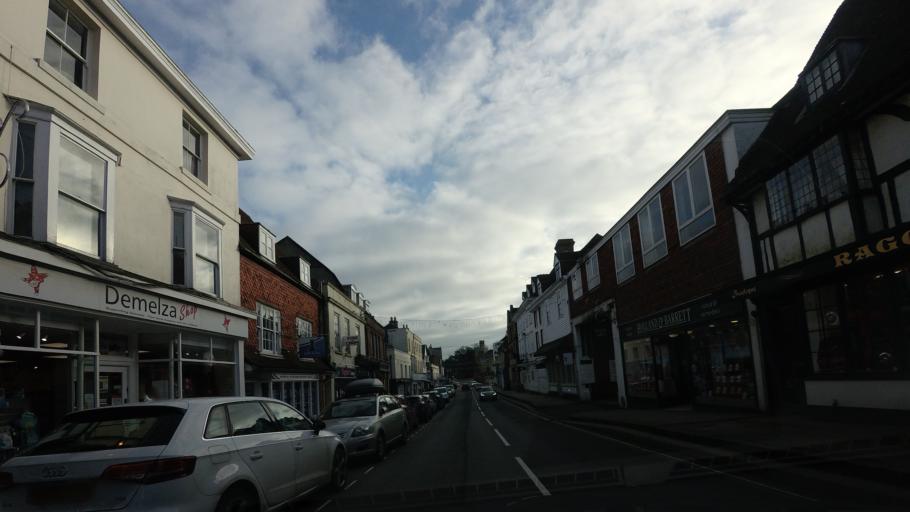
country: GB
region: England
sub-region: East Sussex
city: Battle
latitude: 50.9165
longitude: 0.4847
